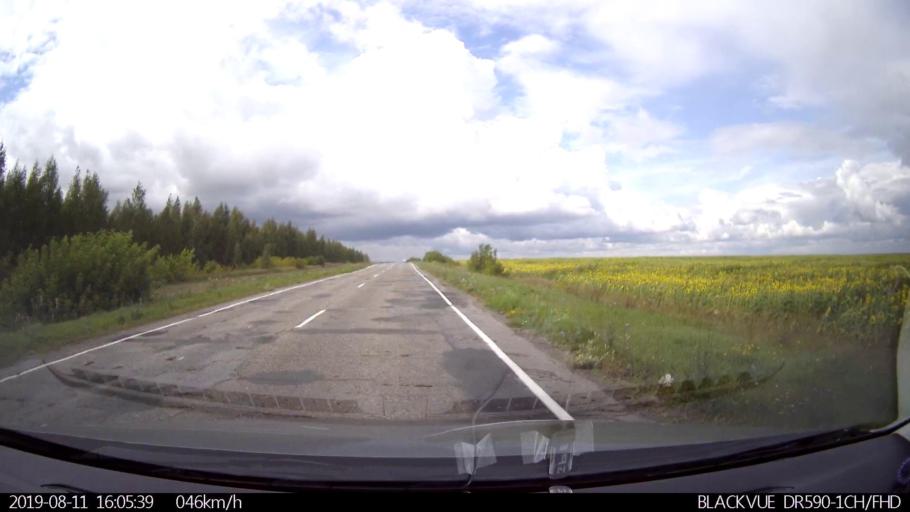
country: RU
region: Ulyanovsk
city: Ignatovka
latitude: 53.9622
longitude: 47.6491
